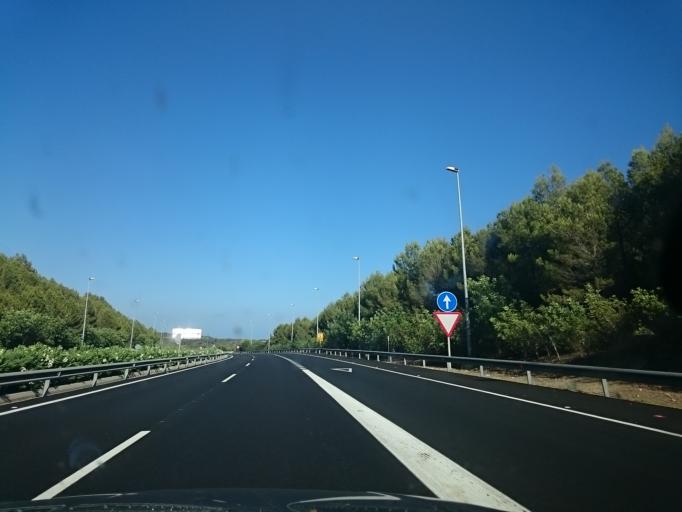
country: ES
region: Catalonia
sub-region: Provincia de Tarragona
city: Cunit
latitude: 41.2123
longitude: 1.6175
